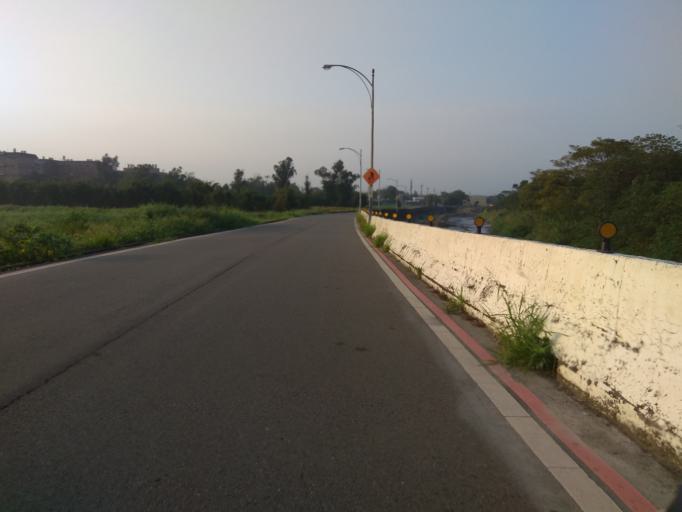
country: TW
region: Taiwan
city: Daxi
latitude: 24.9387
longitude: 121.2119
